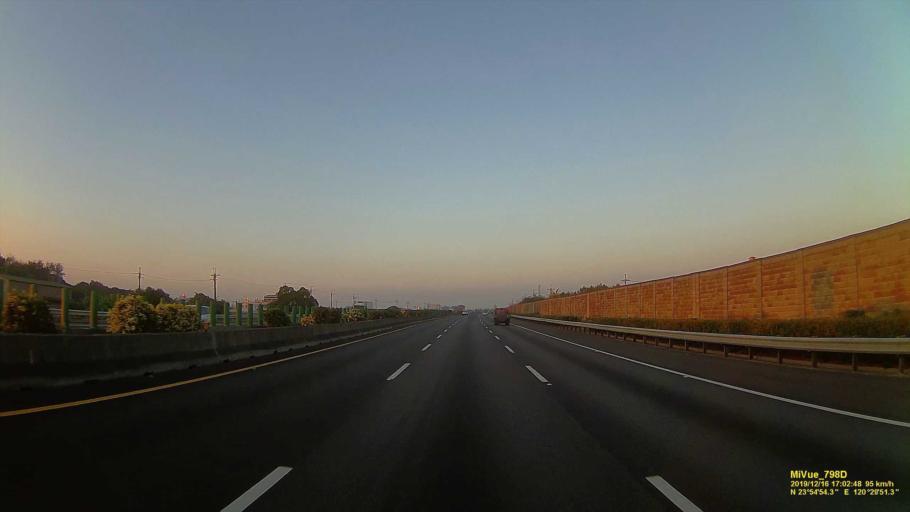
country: TW
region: Taiwan
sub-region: Nantou
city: Nantou
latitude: 23.9156
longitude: 120.4976
